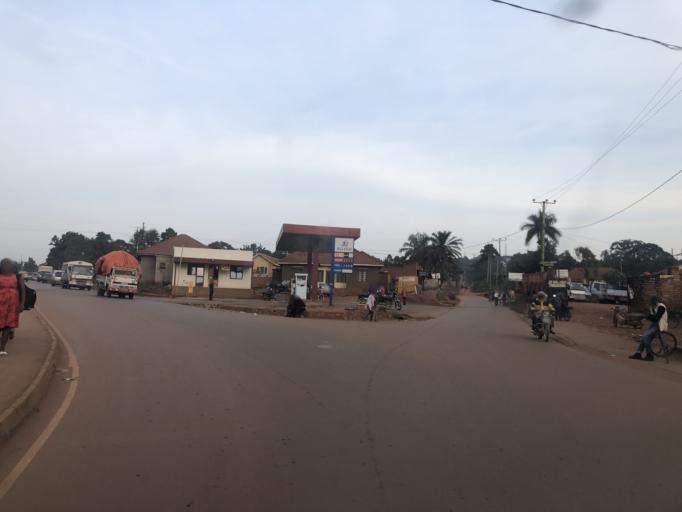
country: UG
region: Central Region
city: Kampala Central Division
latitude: 0.2947
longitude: 32.5278
